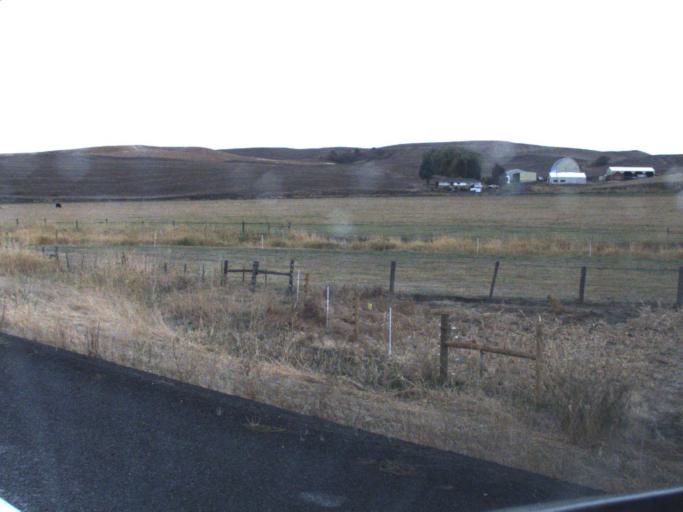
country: US
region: Washington
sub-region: Whitman County
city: Pullman
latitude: 46.5773
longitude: -117.1506
